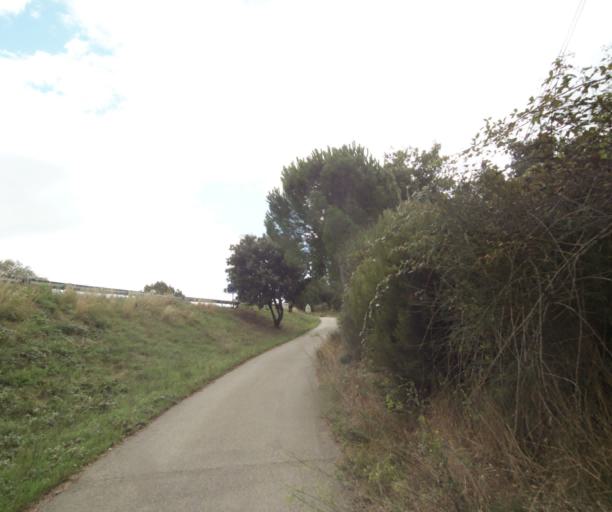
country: FR
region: Languedoc-Roussillon
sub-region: Departement des Pyrenees-Orientales
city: Argelers
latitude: 42.5364
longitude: 3.0310
